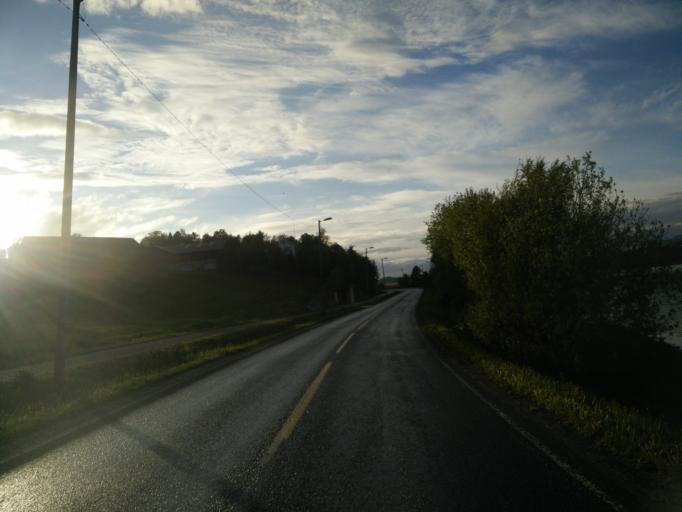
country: NO
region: Sor-Trondelag
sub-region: Skaun
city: Borsa
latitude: 63.3158
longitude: 10.1518
